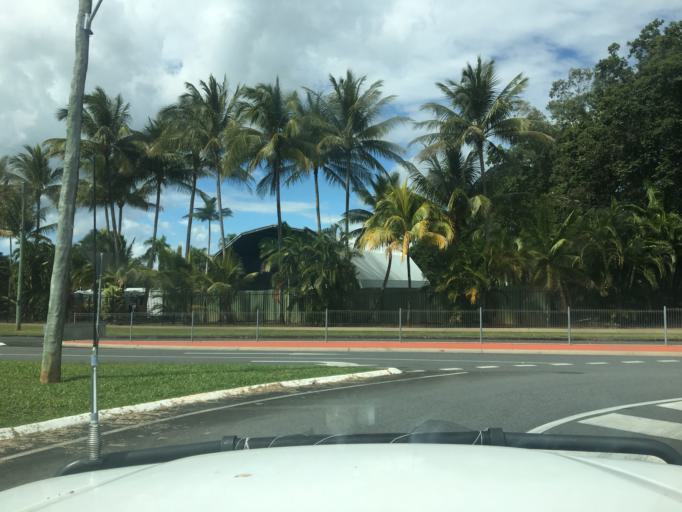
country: AU
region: Queensland
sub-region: Cairns
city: Woree
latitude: -16.9674
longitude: 145.7416
